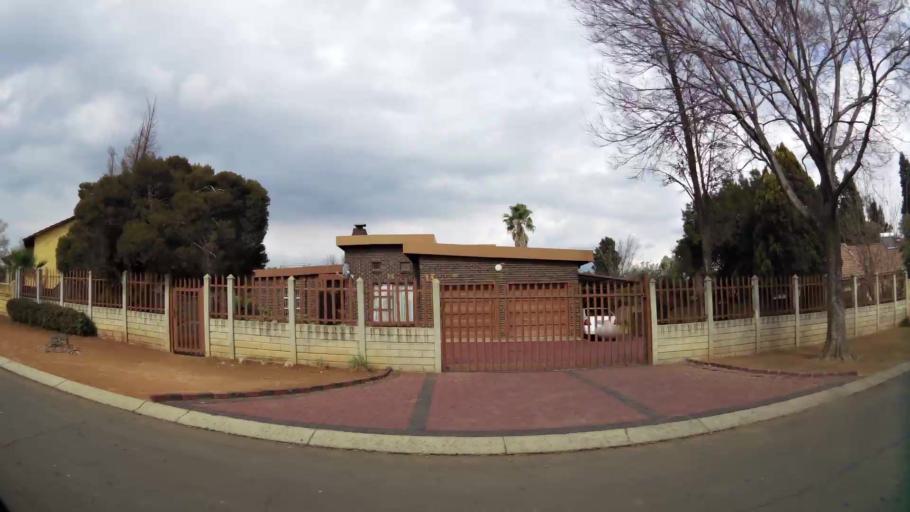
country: ZA
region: Gauteng
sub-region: Sedibeng District Municipality
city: Vanderbijlpark
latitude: -26.7048
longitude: 27.8038
